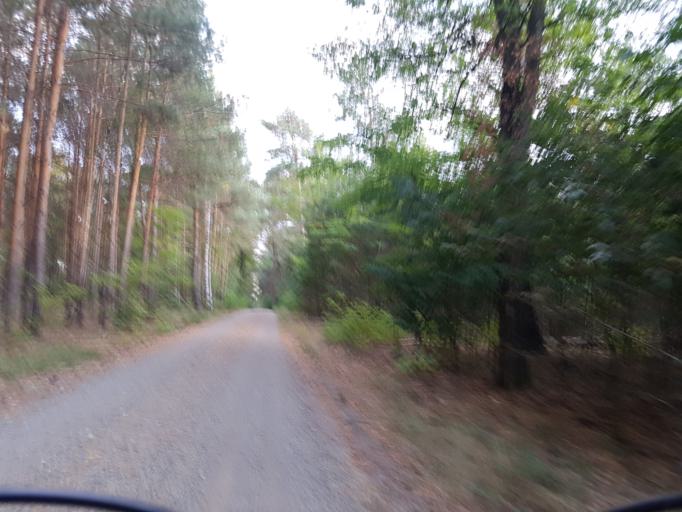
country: DE
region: Brandenburg
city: Trobitz
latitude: 51.5752
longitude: 13.4600
